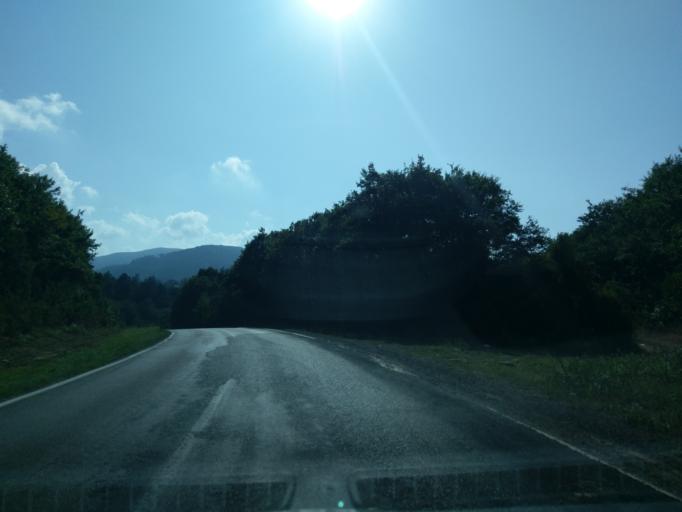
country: TR
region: Sinop
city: Yenikonak
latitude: 41.9442
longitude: 34.7353
